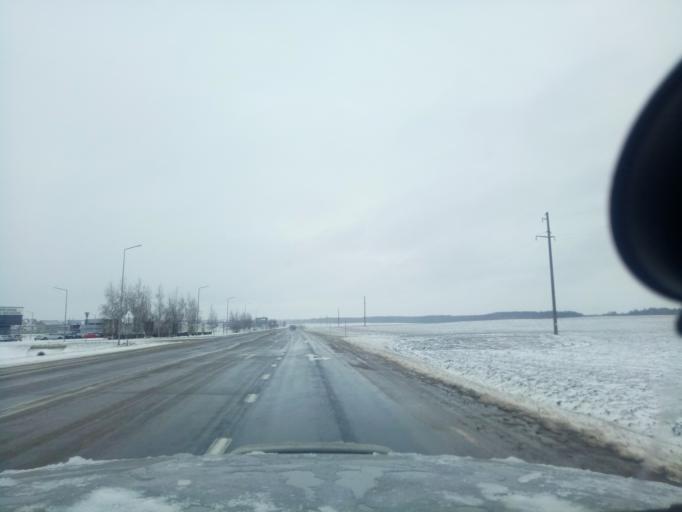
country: BY
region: Minsk
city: Nyasvizh
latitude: 53.2270
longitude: 26.6434
